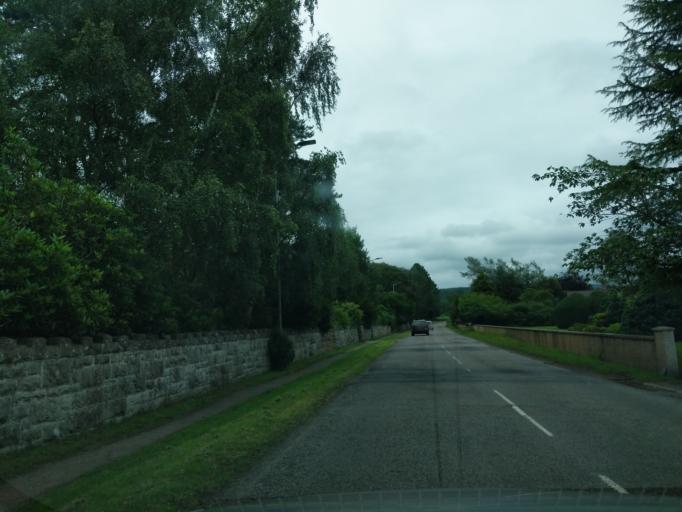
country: GB
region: Scotland
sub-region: Moray
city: Forres
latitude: 57.6027
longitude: -3.5887
